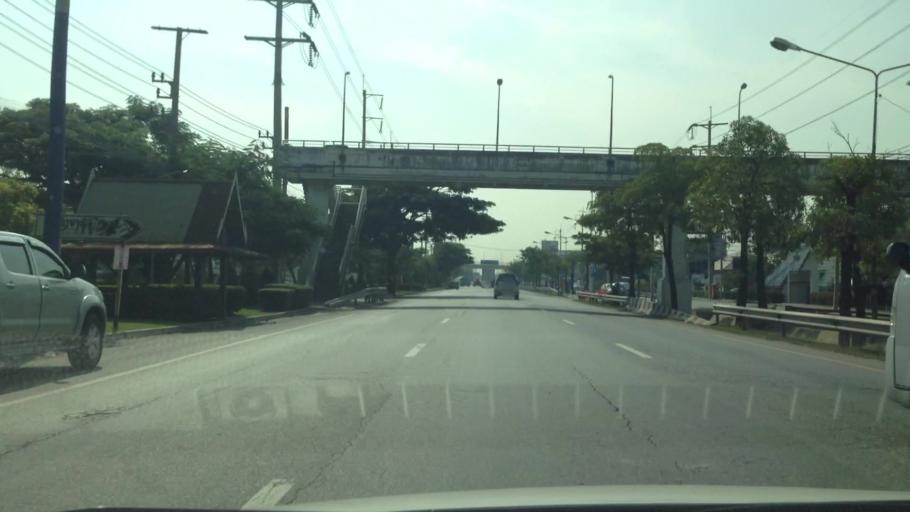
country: TH
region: Samut Prakan
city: Samut Prakan
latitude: 13.5515
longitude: 100.6155
